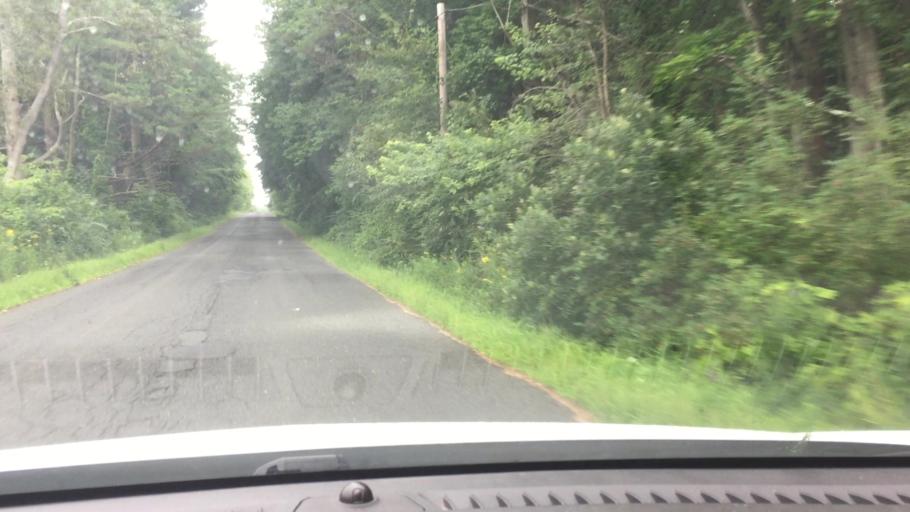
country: US
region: Massachusetts
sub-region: Berkshire County
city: Lee
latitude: 42.3129
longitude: -73.2854
